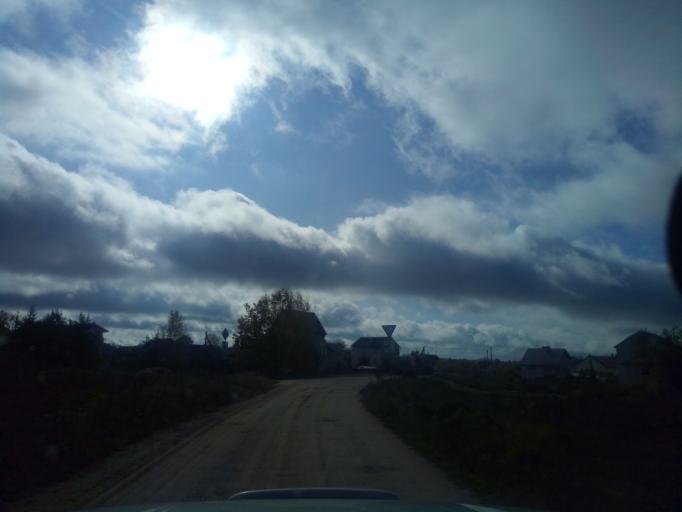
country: BY
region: Minsk
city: Zaslawye
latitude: 54.0176
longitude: 27.2905
